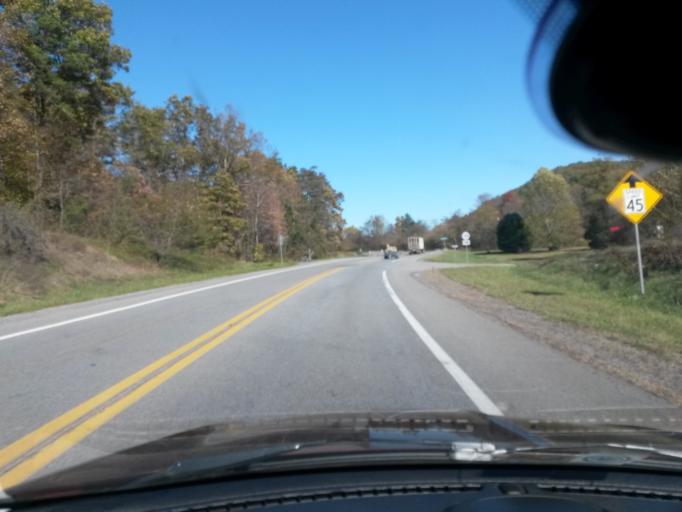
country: US
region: Virginia
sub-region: Alleghany County
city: Clifton Forge
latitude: 37.7782
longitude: -79.7814
